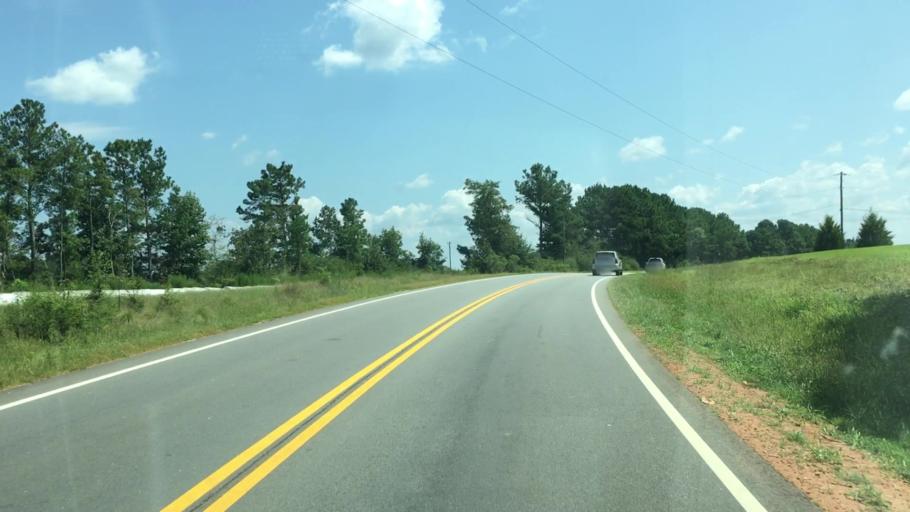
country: US
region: Georgia
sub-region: Oconee County
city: Watkinsville
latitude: 33.8072
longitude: -83.4281
